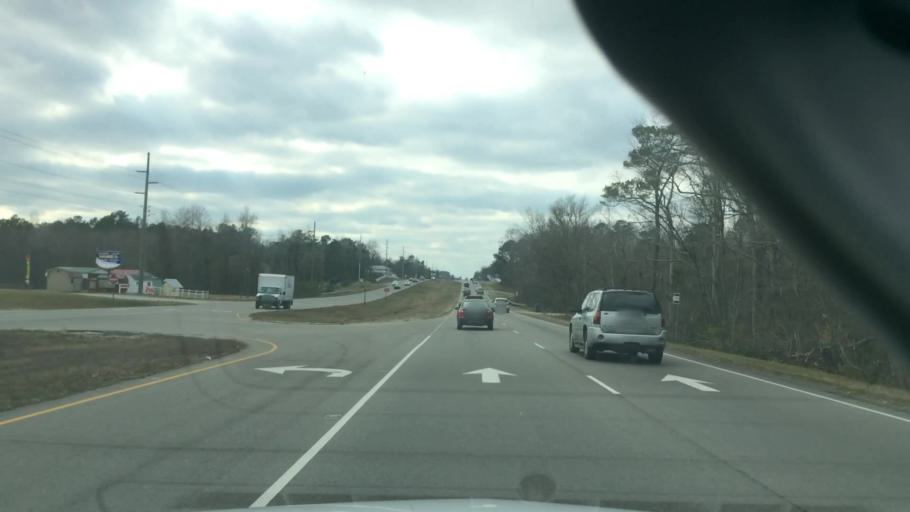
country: US
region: North Carolina
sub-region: Brunswick County
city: Shallotte
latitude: 34.0129
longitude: -78.2859
